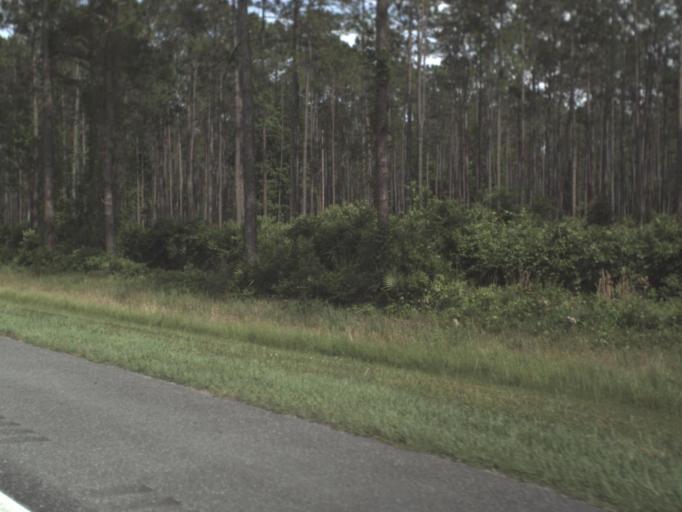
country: US
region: Florida
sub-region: Columbia County
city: Watertown
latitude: 30.2576
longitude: -82.4864
